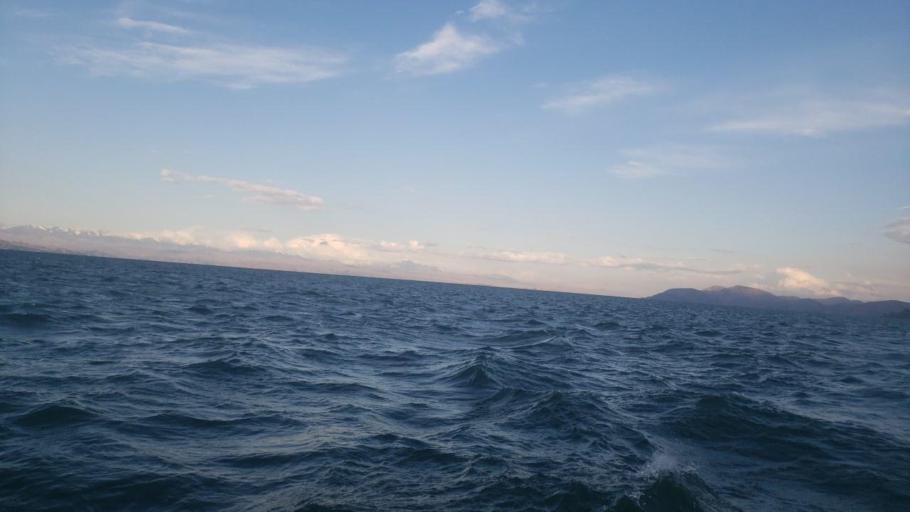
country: BO
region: La Paz
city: San Pedro
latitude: -16.2764
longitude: -68.7858
